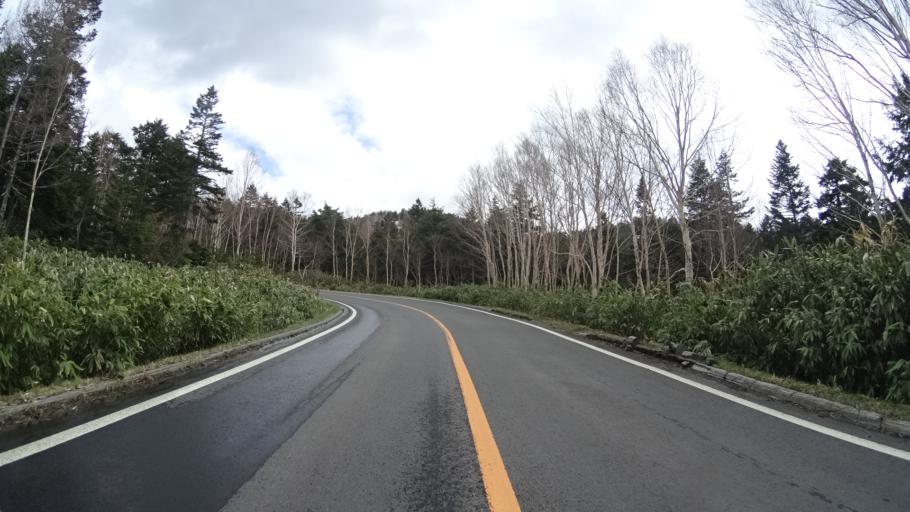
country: JP
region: Nagano
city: Nakano
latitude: 36.6764
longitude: 138.5075
